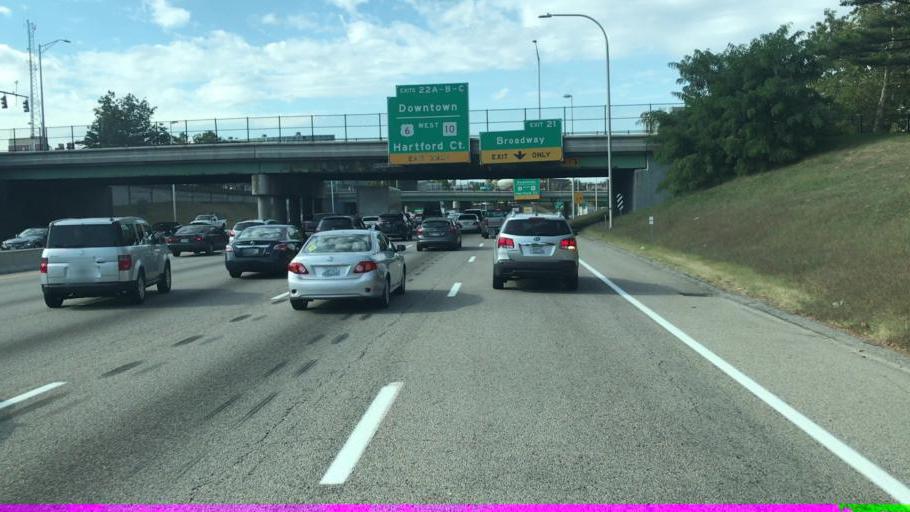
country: US
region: Rhode Island
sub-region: Providence County
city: Providence
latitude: 41.8187
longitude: -71.4178
